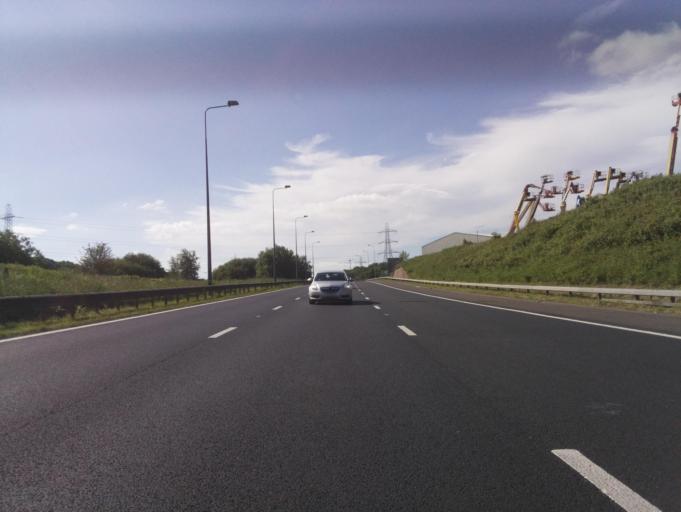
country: GB
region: England
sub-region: Borough of Bolton
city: Kearsley
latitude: 53.5348
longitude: -2.3887
